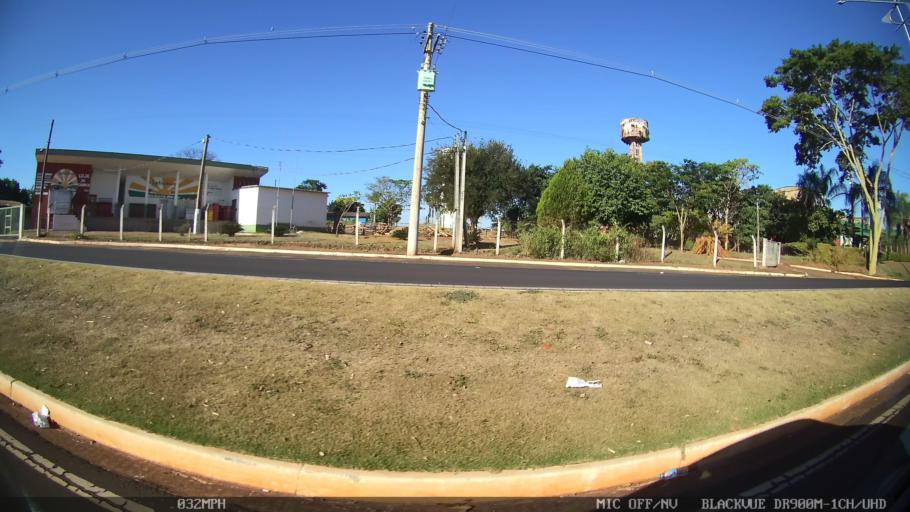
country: BR
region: Sao Paulo
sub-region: Olimpia
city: Olimpia
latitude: -20.7263
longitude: -48.9055
